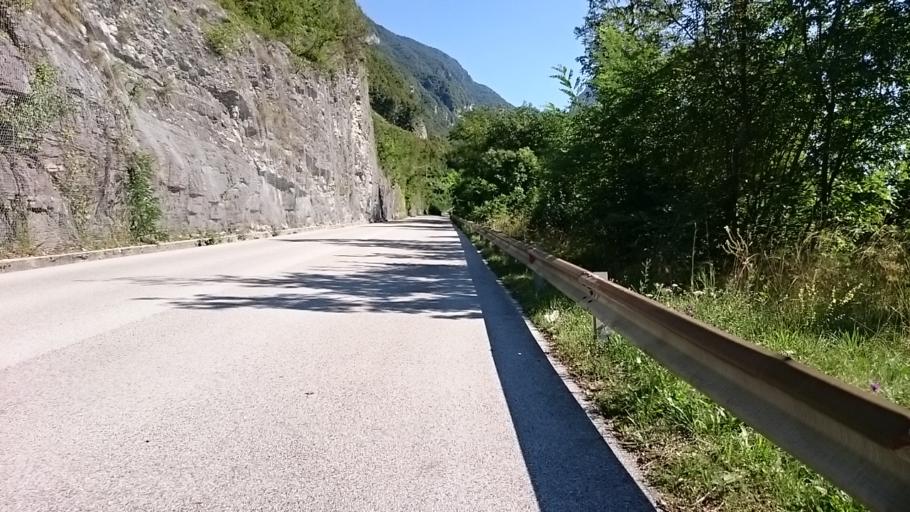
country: IT
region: Veneto
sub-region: Provincia di Belluno
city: Longarone
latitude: 46.2664
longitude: 12.3119
